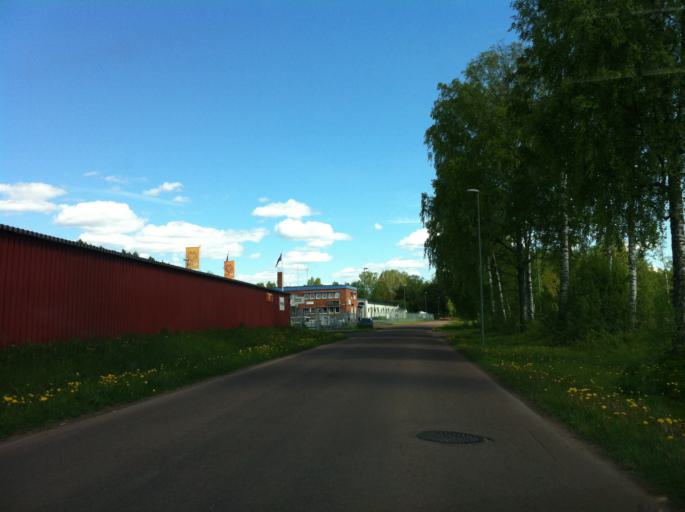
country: SE
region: Dalarna
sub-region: Mora Kommun
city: Mora
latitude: 61.0076
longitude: 14.5557
